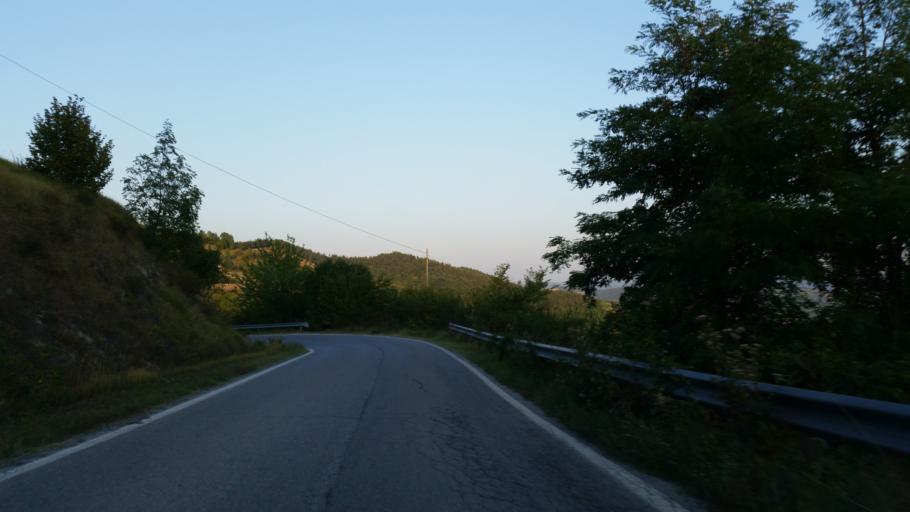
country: IT
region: Piedmont
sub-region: Provincia di Cuneo
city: Borgomale
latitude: 44.6527
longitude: 8.1331
